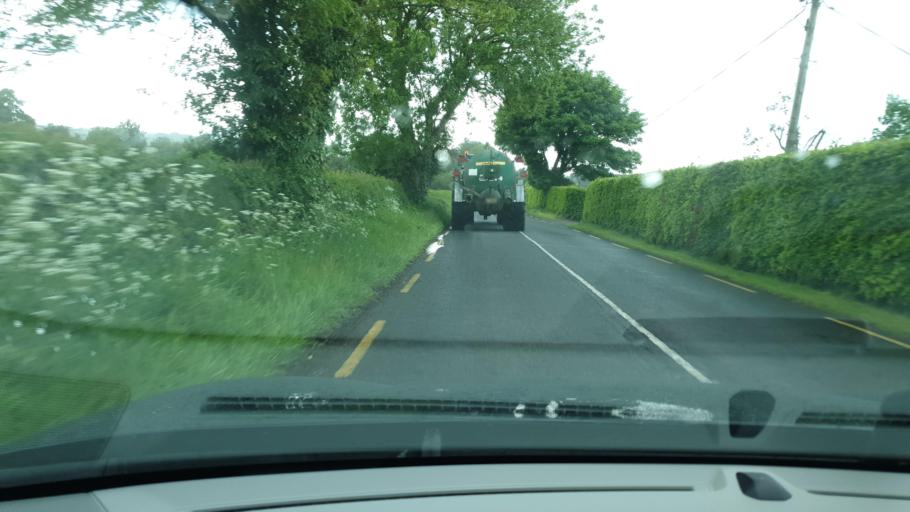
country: IE
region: Leinster
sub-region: Laois
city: Mountrath
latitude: 53.0538
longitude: -7.4056
